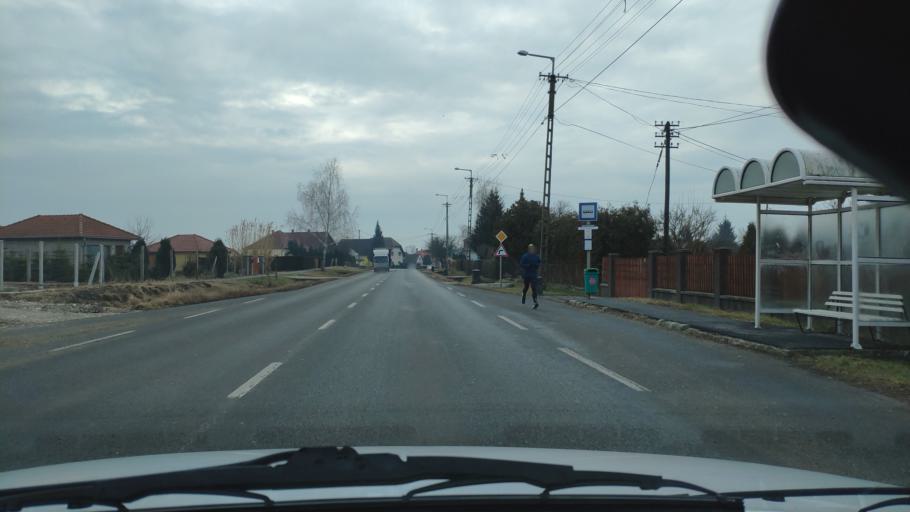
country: HU
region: Zala
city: Nagykanizsa
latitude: 46.5046
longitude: 16.9862
